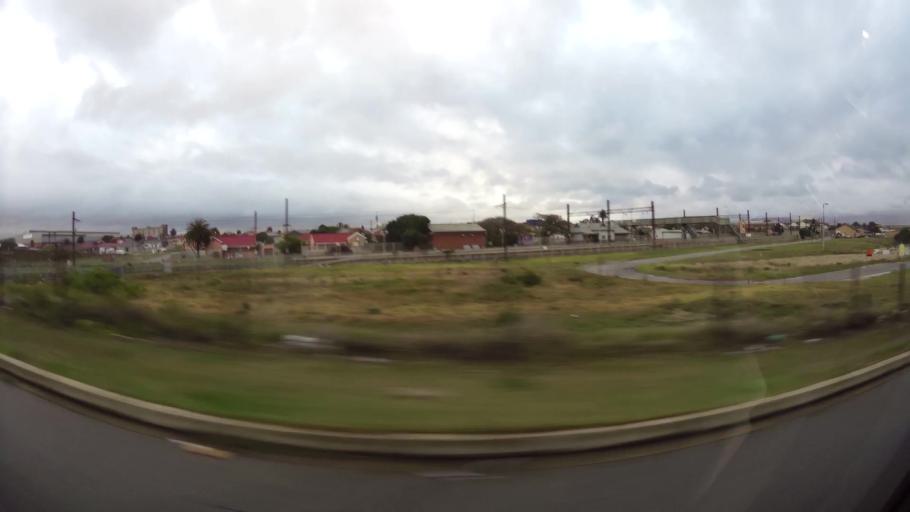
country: ZA
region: Eastern Cape
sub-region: Nelson Mandela Bay Metropolitan Municipality
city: Port Elizabeth
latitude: -33.9244
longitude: 25.6056
